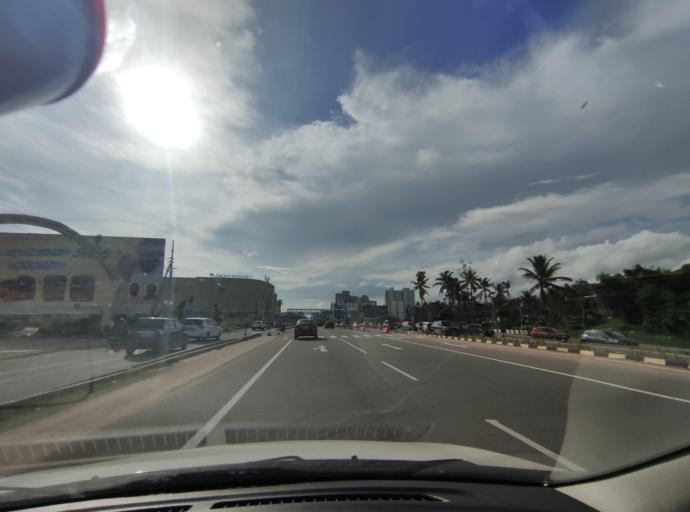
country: IN
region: Kerala
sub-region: Thiruvananthapuram
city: Thiruvananthapuram
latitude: 8.5136
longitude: 76.9005
